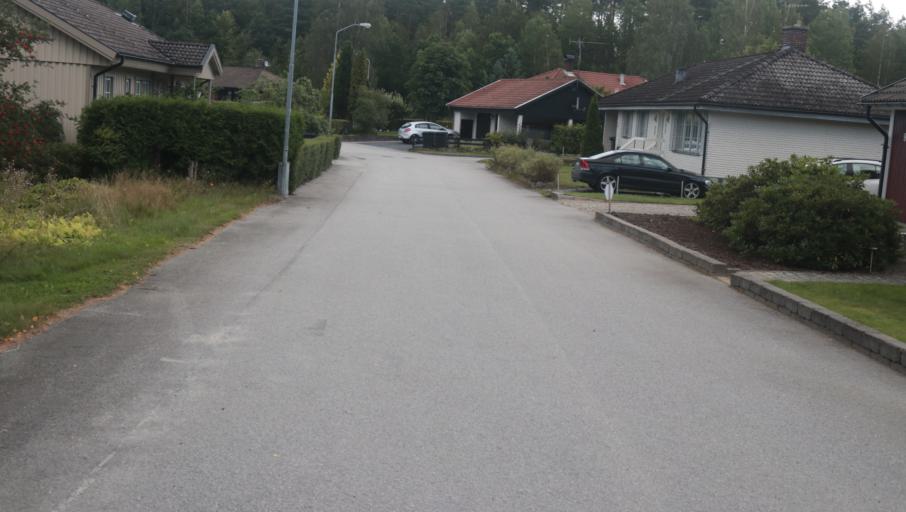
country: SE
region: Blekinge
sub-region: Karlshamns Kommun
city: Svangsta
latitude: 56.2688
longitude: 14.7734
